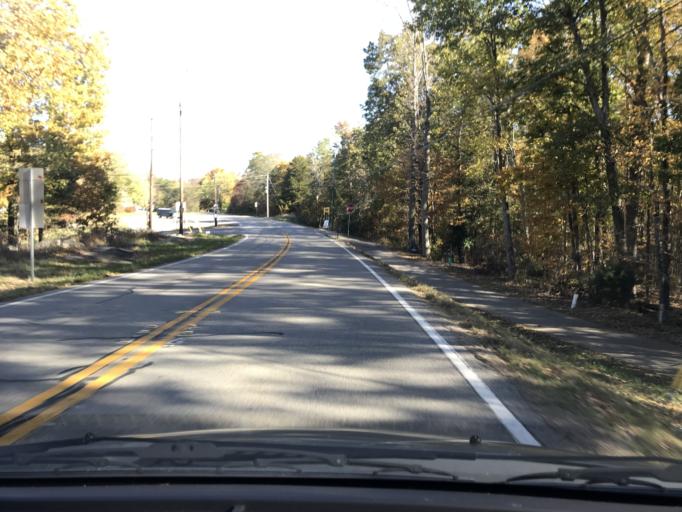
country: US
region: Georgia
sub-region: Dade County
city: Trenton
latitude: 34.9019
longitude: -85.4390
